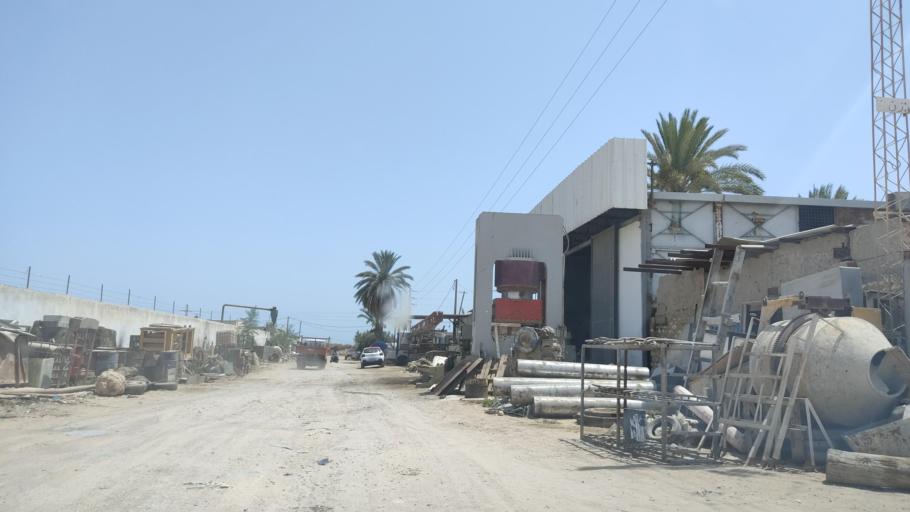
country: TN
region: Safaqis
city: Sfax
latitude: 34.7104
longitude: 10.7289
